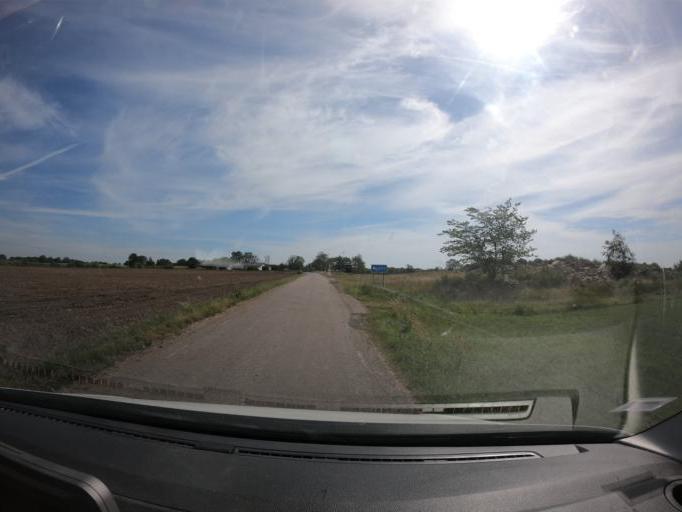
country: SE
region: Skane
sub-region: Angelholms Kommun
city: Vejbystrand
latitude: 56.4177
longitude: 12.6647
